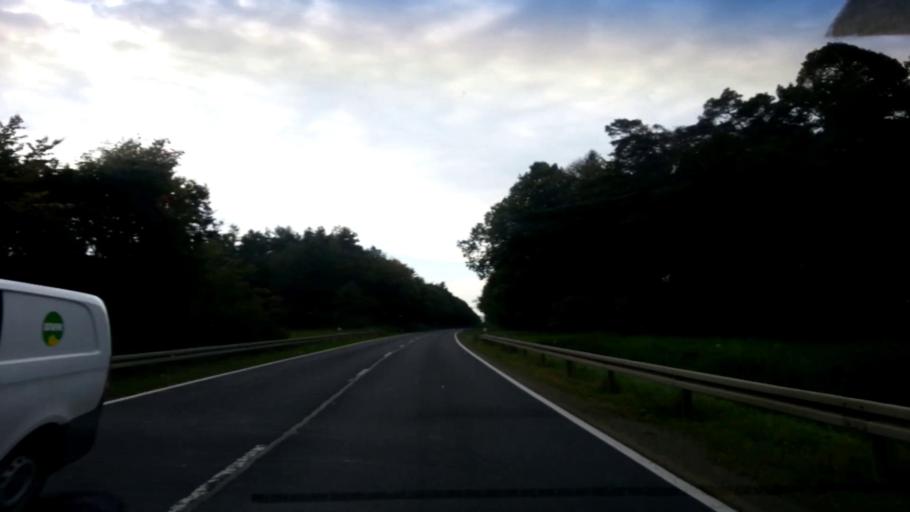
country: DE
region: Bavaria
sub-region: Regierungsbezirk Unterfranken
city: Wonfurt
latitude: 49.9969
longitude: 10.4394
